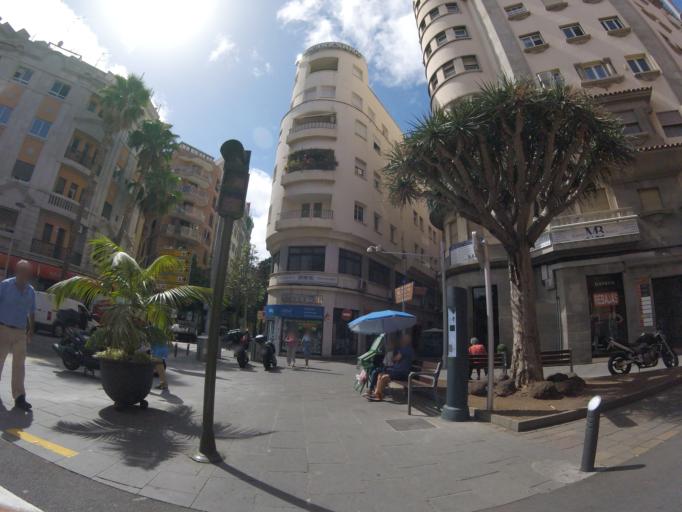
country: ES
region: Canary Islands
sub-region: Provincia de Santa Cruz de Tenerife
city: Santa Cruz de Tenerife
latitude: 28.4688
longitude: -16.2515
